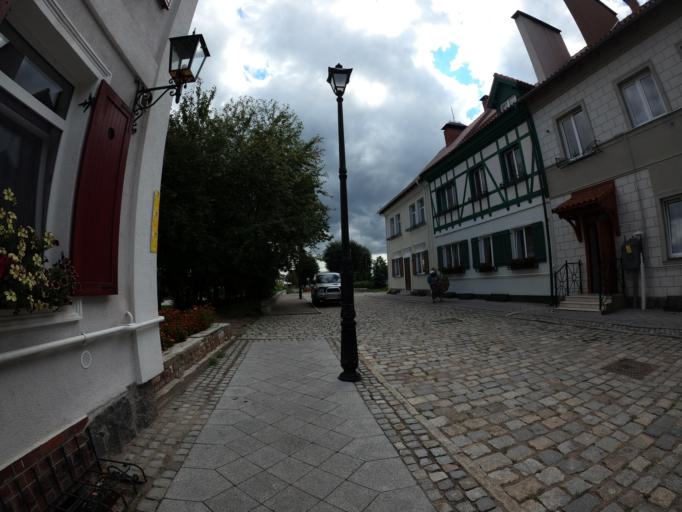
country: RU
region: Kaliningrad
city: Zheleznodorozhnyy
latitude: 54.3619
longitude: 21.3055
